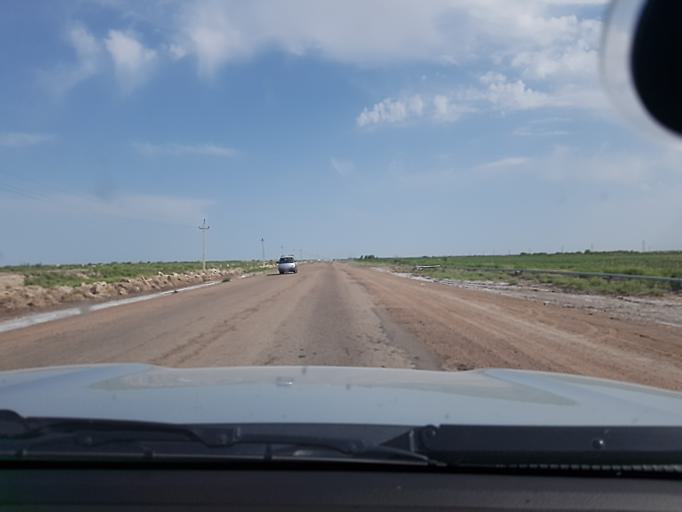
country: TM
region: Dasoguz
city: Boldumsaz
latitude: 42.0776
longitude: 59.7420
